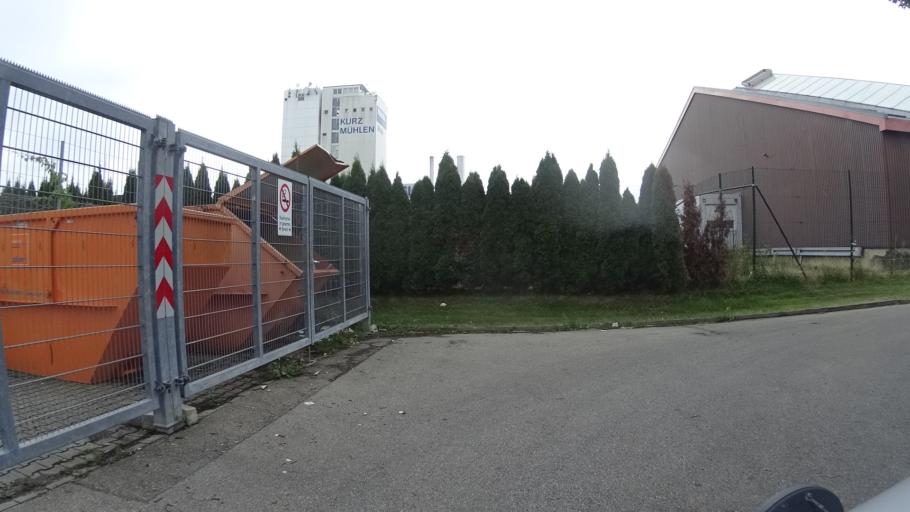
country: DE
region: Bavaria
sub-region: Swabia
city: Memmingen
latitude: 48.0026
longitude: 10.1687
